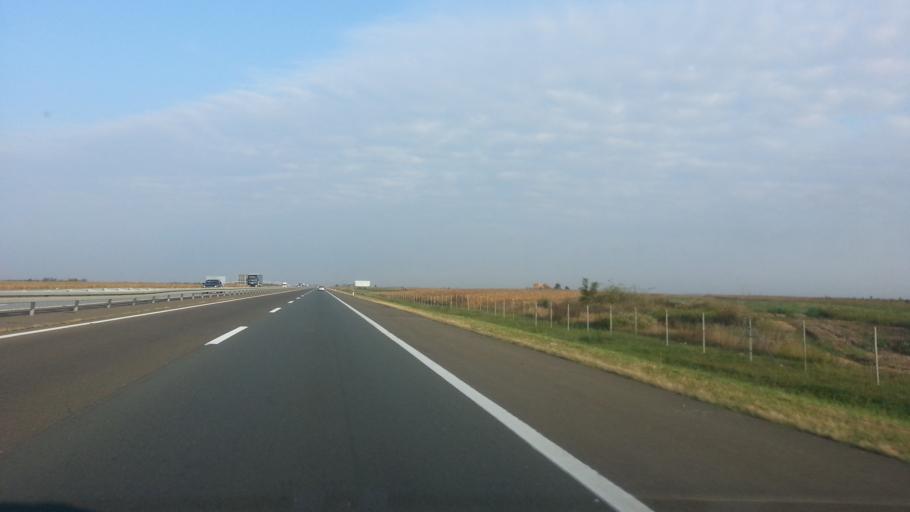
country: RS
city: Novi Banovci
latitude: 44.9513
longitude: 20.2677
